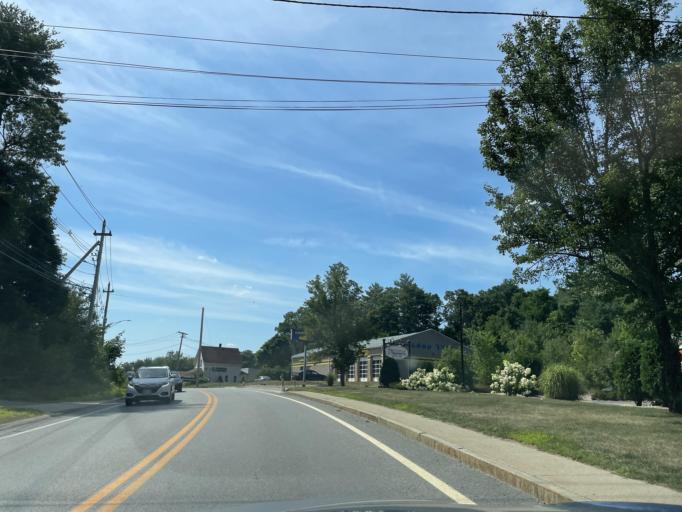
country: US
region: Massachusetts
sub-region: Norfolk County
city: Franklin
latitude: 42.0796
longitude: -71.3718
